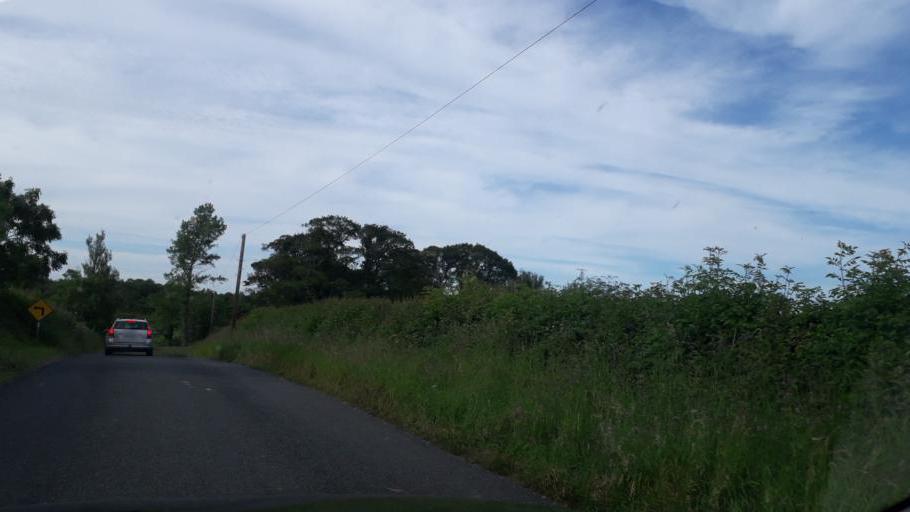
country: IE
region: Leinster
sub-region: Loch Garman
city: Courtown
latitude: 52.5417
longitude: -6.2534
